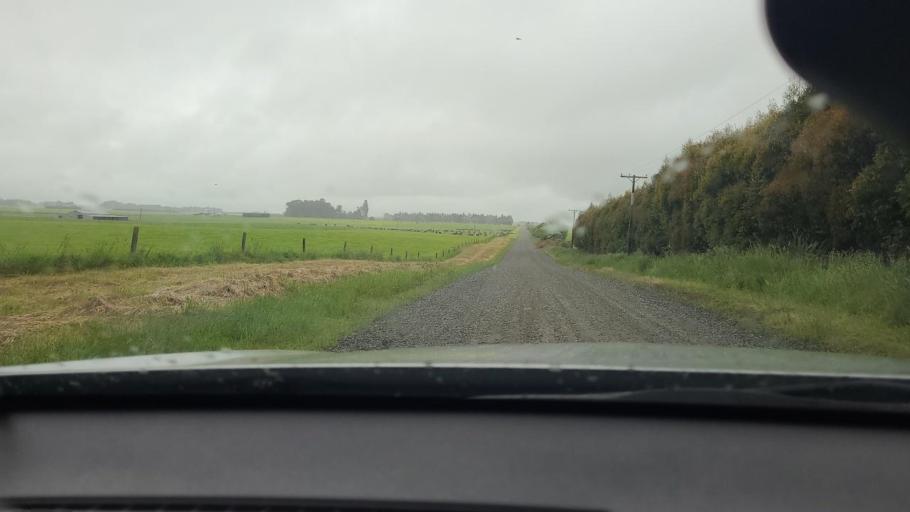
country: NZ
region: Southland
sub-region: Southland District
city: Riverton
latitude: -46.2061
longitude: 168.1115
